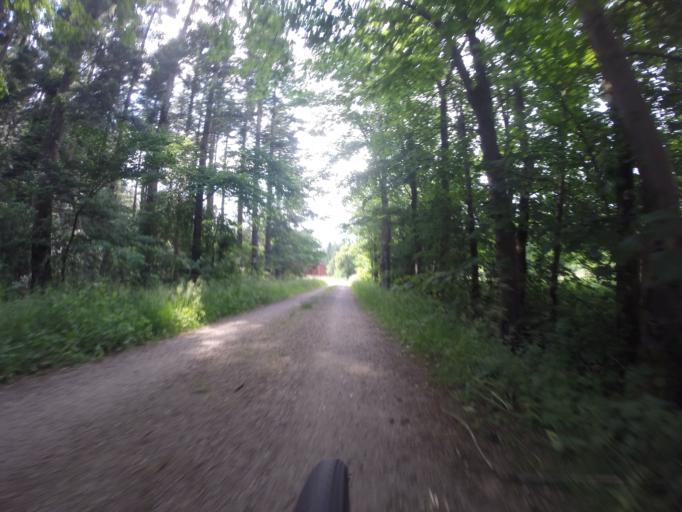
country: DK
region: Capital Region
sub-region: Ballerup Kommune
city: Ballerup
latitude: 55.6971
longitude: 12.3389
